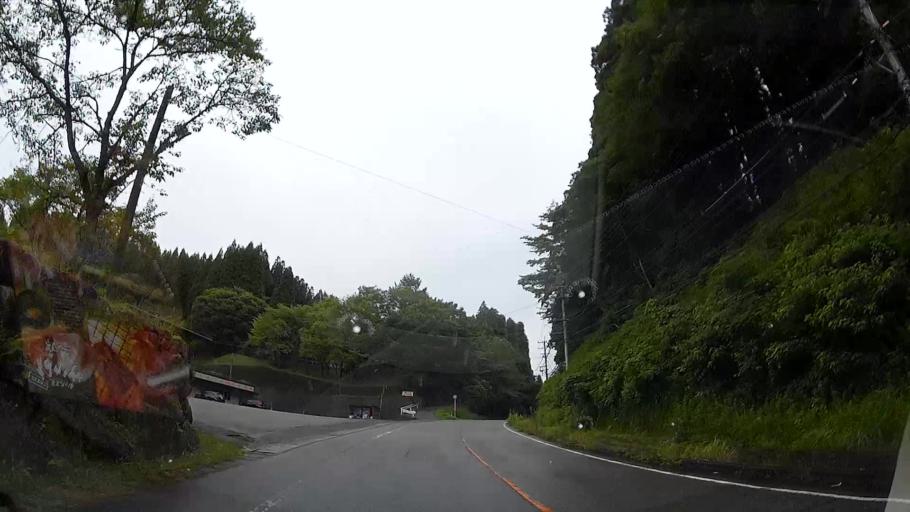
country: JP
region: Oita
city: Tsukawaki
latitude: 33.1408
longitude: 131.0616
